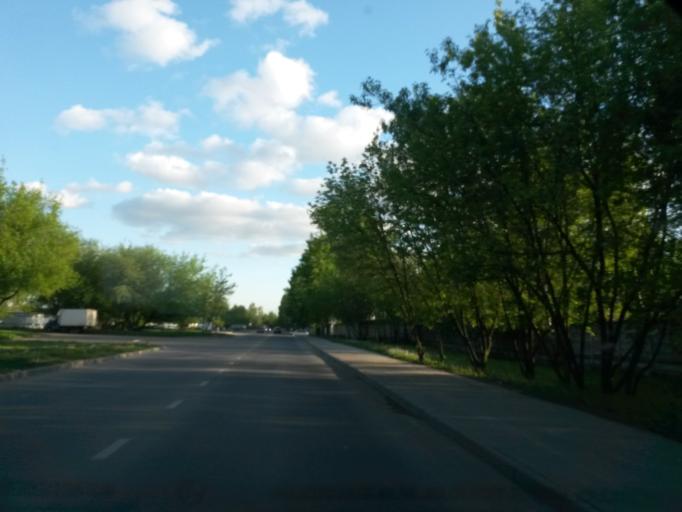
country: RU
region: Moscow
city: Solntsevo
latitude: 55.6465
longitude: 37.3845
